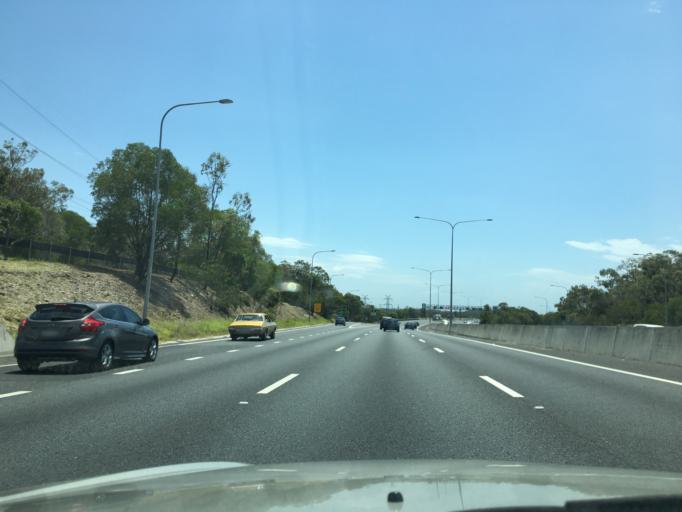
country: AU
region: Queensland
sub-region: Brisbane
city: Belmont
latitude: -27.5080
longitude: 153.1250
